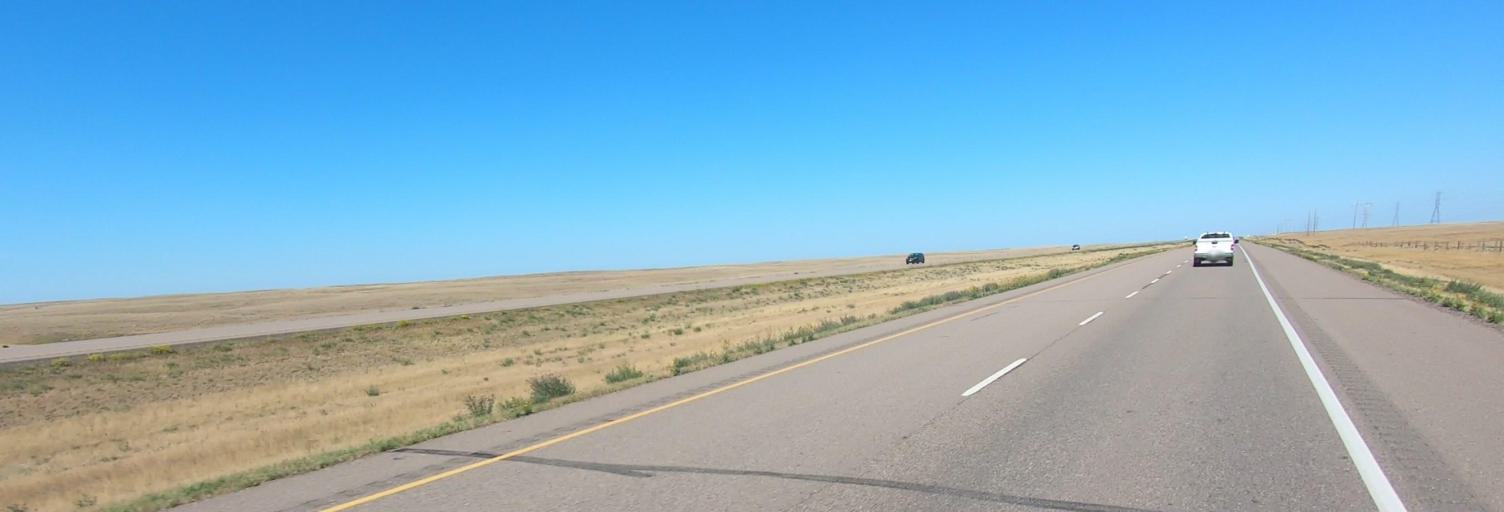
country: CA
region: Alberta
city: Bow Island
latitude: 50.3009
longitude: -111.3161
